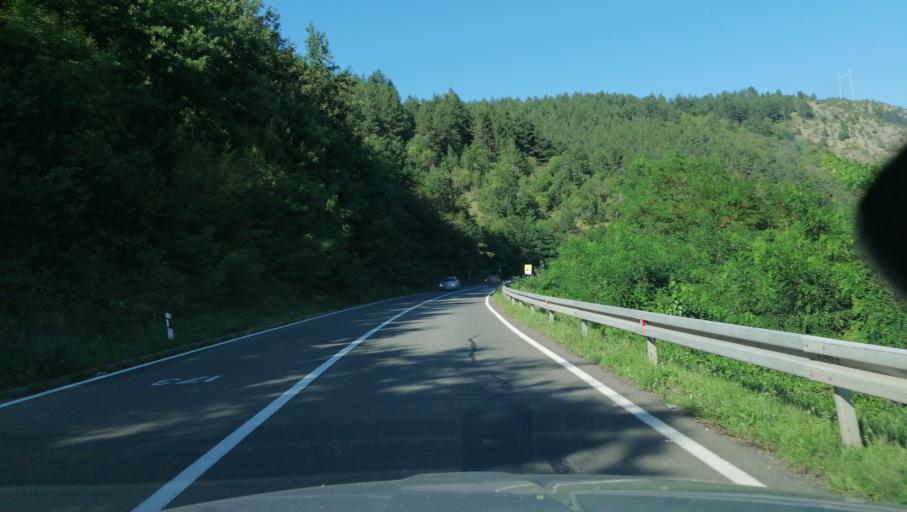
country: RS
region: Central Serbia
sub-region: Raski Okrug
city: Kraljevo
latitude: 43.6655
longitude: 20.5675
